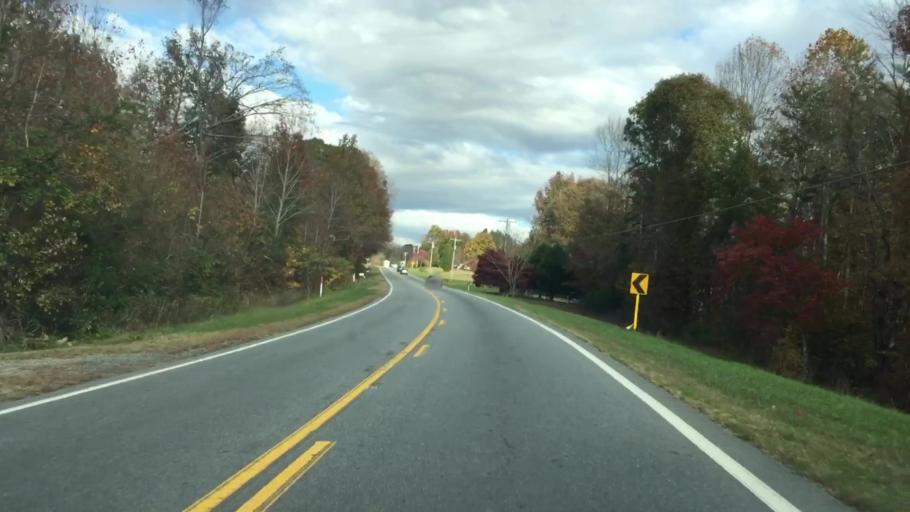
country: US
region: North Carolina
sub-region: Guilford County
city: Stokesdale
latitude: 36.2331
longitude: -80.0138
